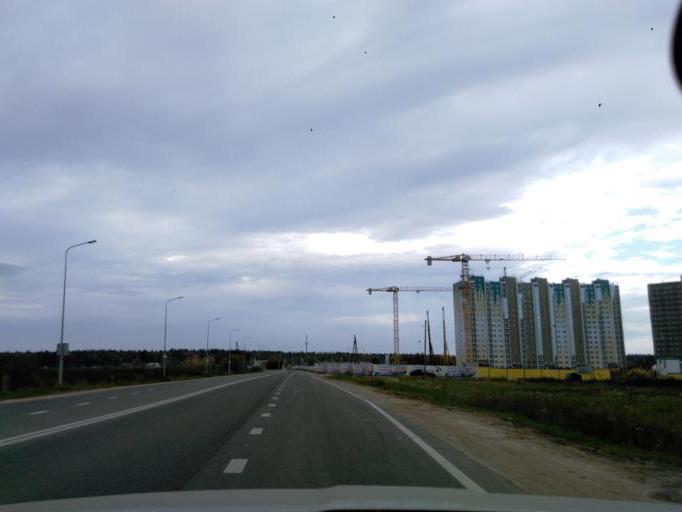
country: RU
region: Moskovskaya
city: Andreyevka
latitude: 55.9747
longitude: 37.1052
